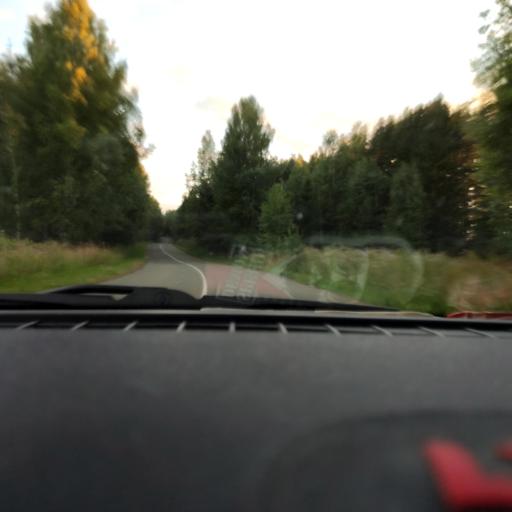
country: RU
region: Perm
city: Ocher
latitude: 57.9351
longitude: 54.7935
